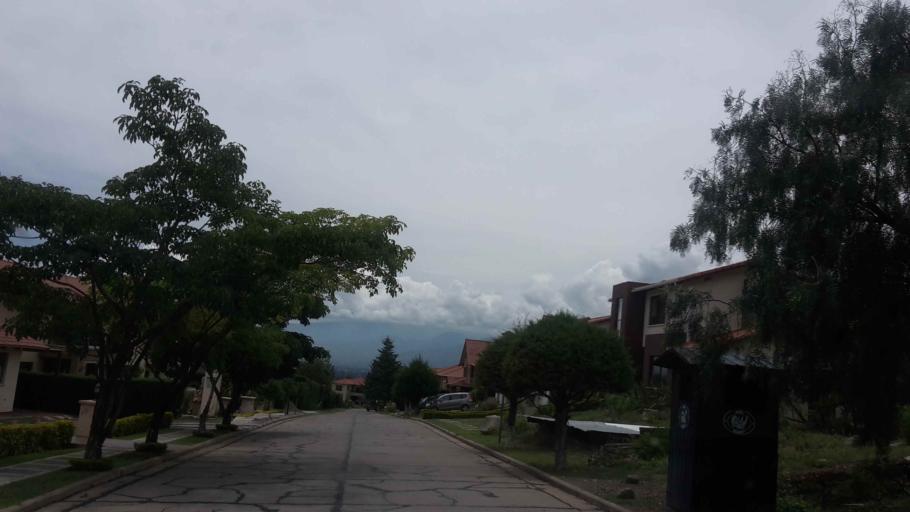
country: BO
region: Cochabamba
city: Cochabamba
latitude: -17.3378
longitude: -66.1846
